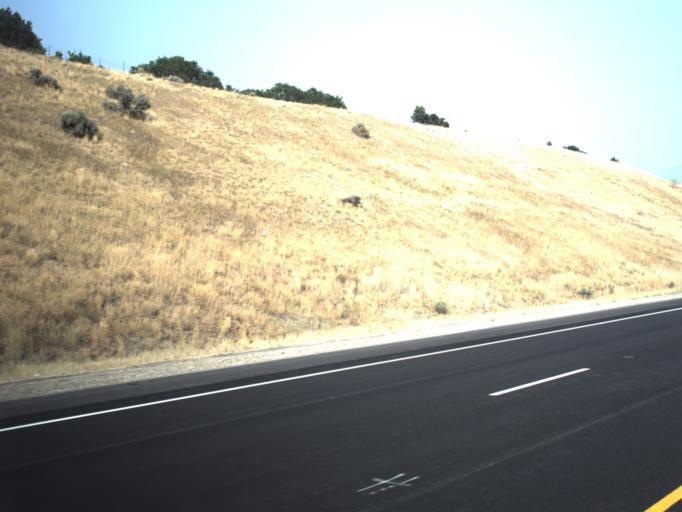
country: US
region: Utah
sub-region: Summit County
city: Kamas
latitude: 40.6357
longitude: -111.3399
